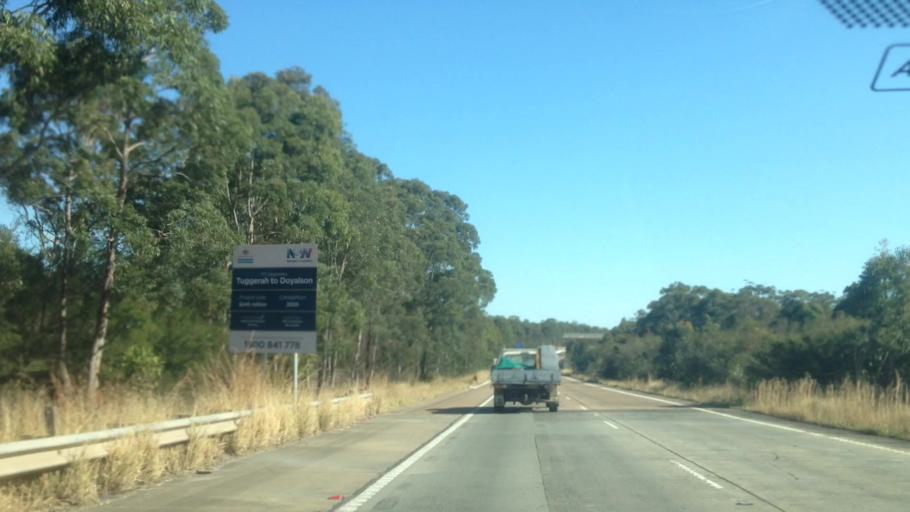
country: AU
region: New South Wales
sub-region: Wyong Shire
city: Jilliby
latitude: -33.2101
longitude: 151.4534
